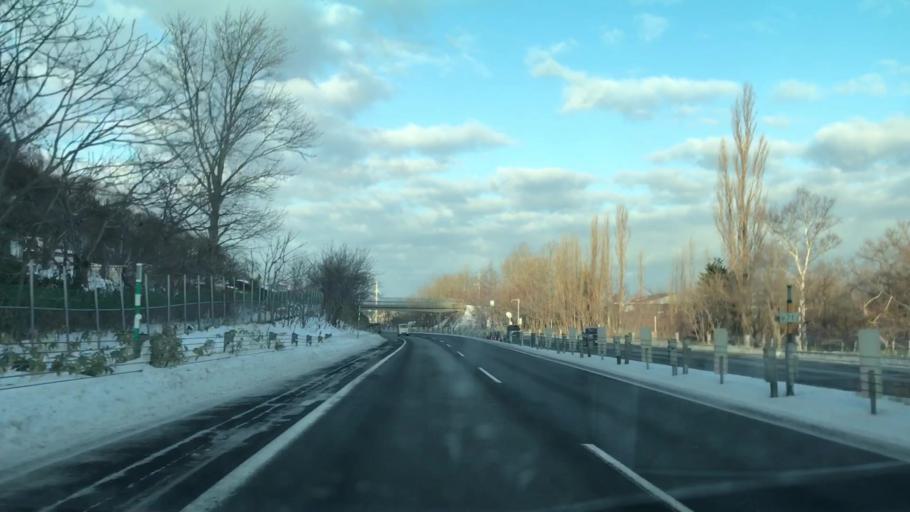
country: JP
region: Hokkaido
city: Sapporo
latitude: 43.1272
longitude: 141.1953
